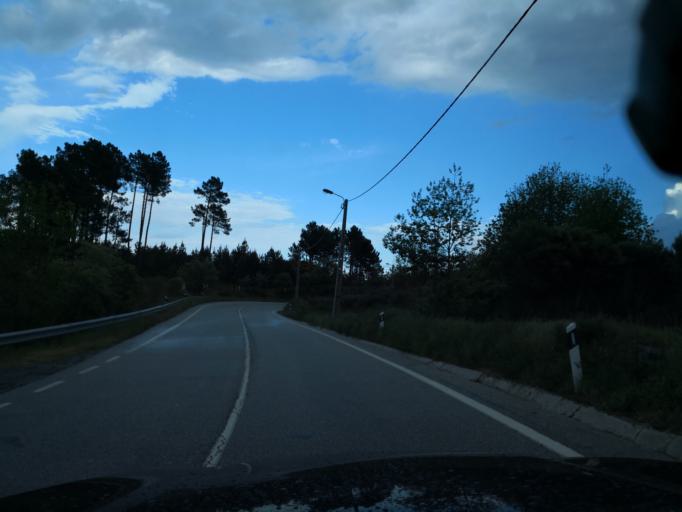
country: PT
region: Vila Real
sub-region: Vila Real
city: Vila Real
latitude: 41.3756
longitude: -7.7183
